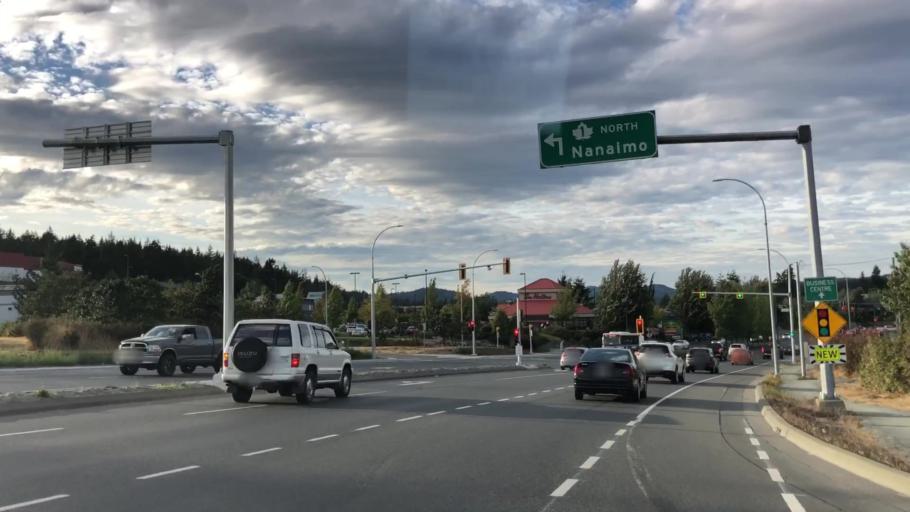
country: CA
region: British Columbia
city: Langford
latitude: 48.4578
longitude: -123.4974
